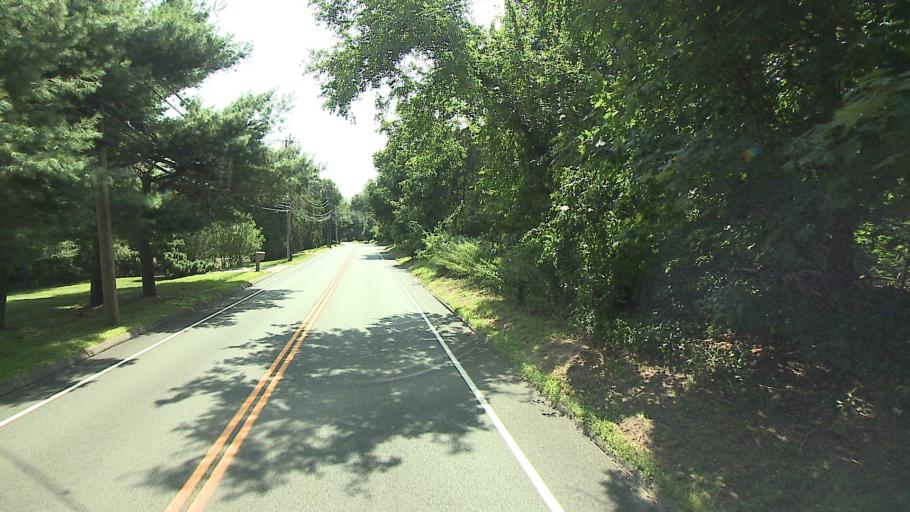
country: US
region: Connecticut
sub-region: Fairfield County
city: Trumbull
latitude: 41.2298
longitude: -73.2617
